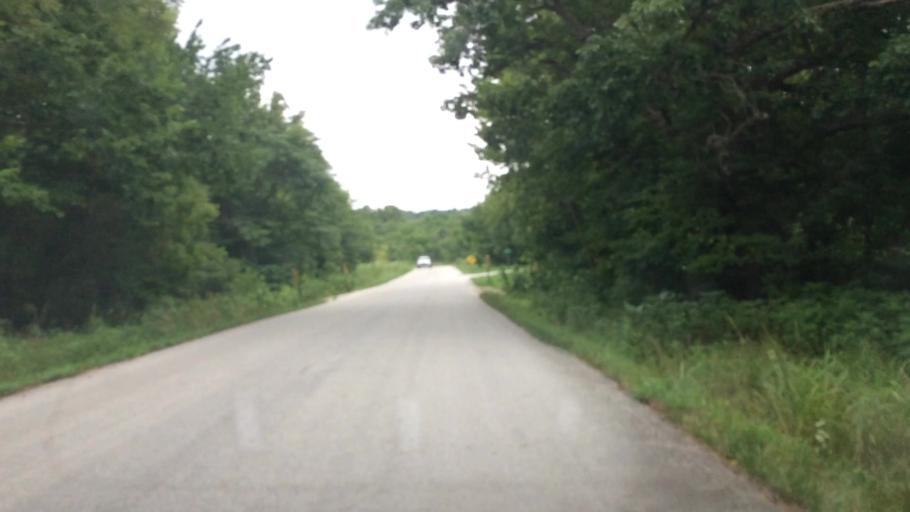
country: US
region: Missouri
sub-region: Greene County
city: Strafford
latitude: 37.3252
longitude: -93.0568
